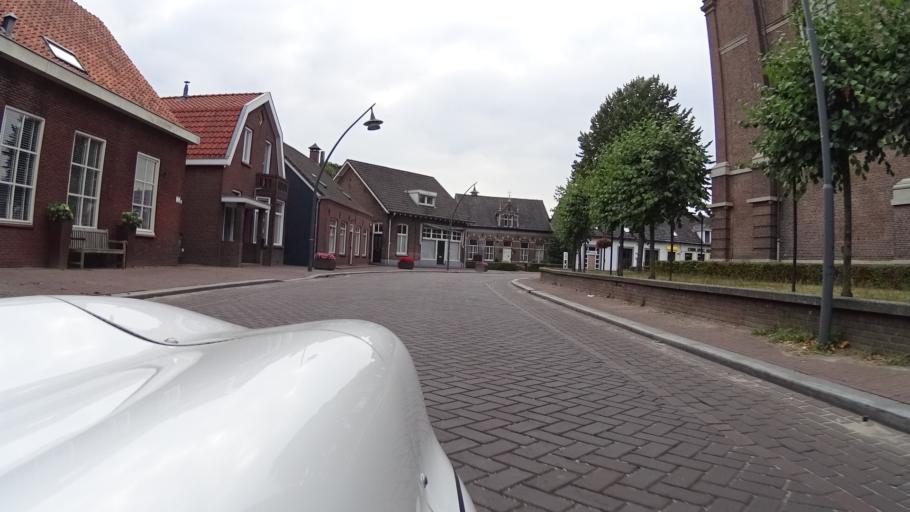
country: NL
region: North Brabant
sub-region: Gemeente Veghel
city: Erp
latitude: 51.5997
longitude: 5.6068
